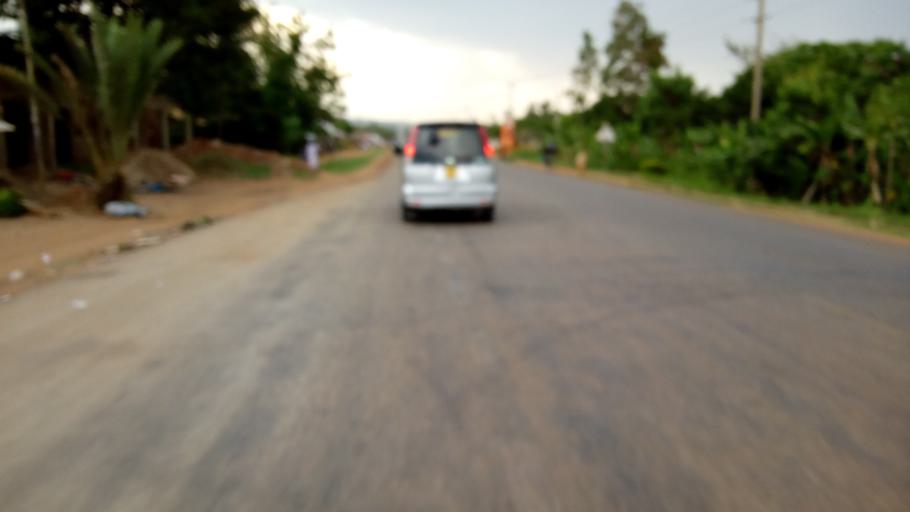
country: UG
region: Eastern Region
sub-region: Mbale District
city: Mbale
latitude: 1.1239
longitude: 34.1687
